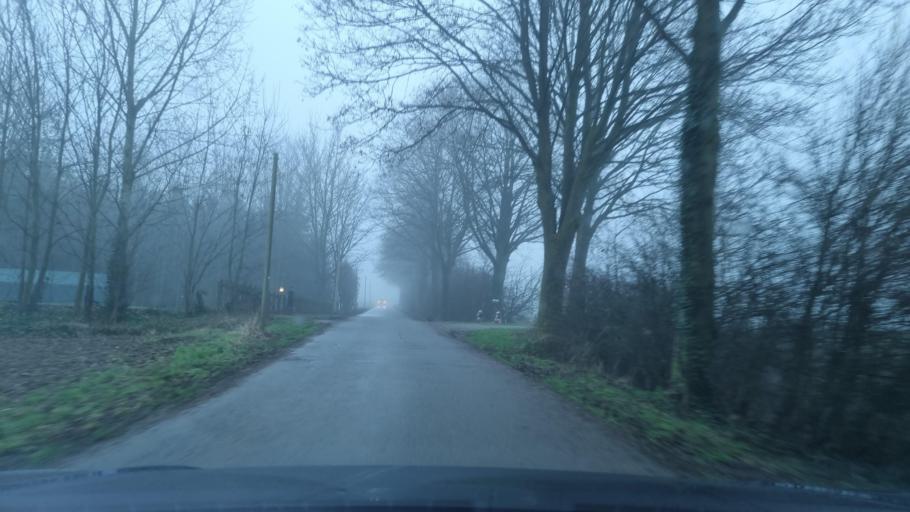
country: DE
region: North Rhine-Westphalia
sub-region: Regierungsbezirk Dusseldorf
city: Emmerich
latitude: 51.8011
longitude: 6.2442
